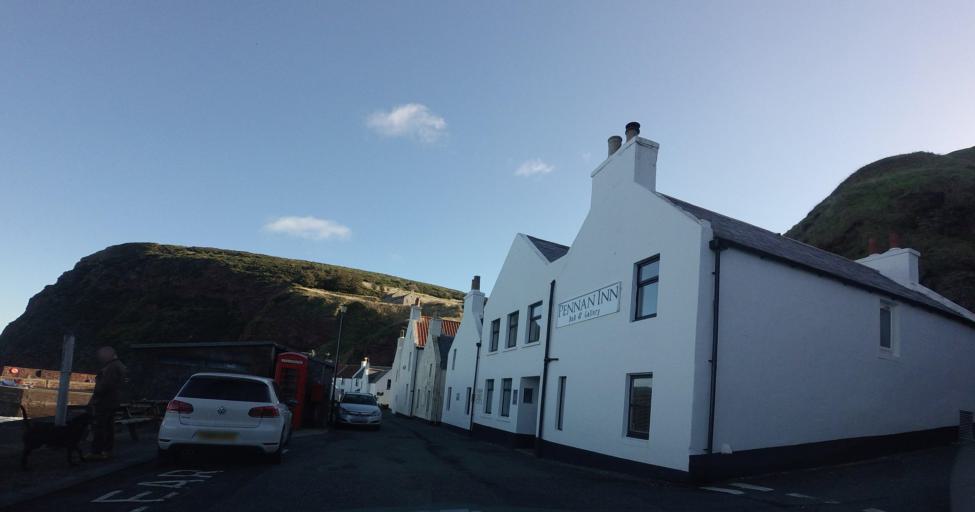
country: GB
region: Scotland
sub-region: Aberdeenshire
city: Rosehearty
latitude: 57.6788
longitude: -2.2598
